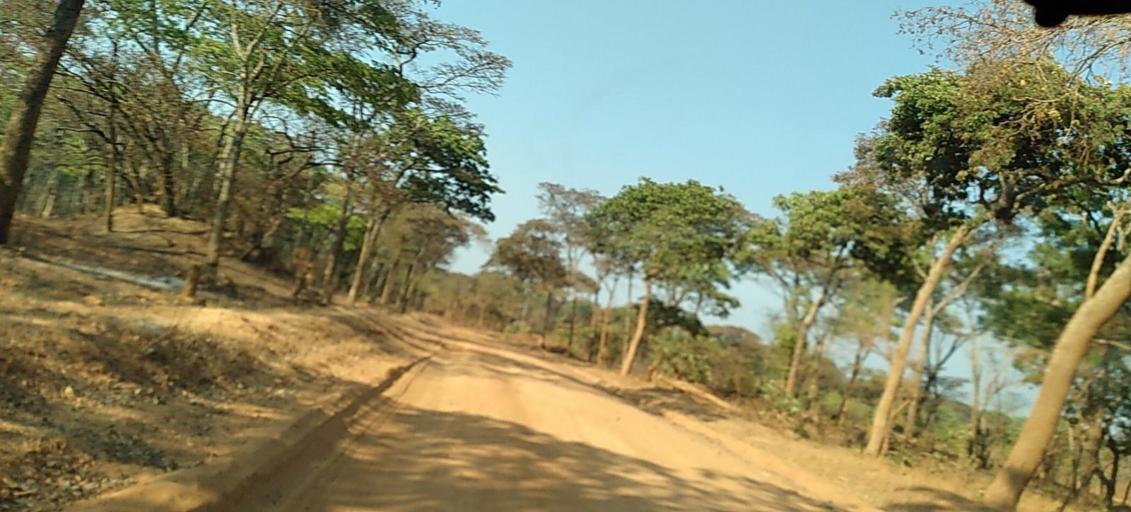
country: ZM
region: North-Western
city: Kasempa
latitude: -13.6022
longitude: 25.9783
